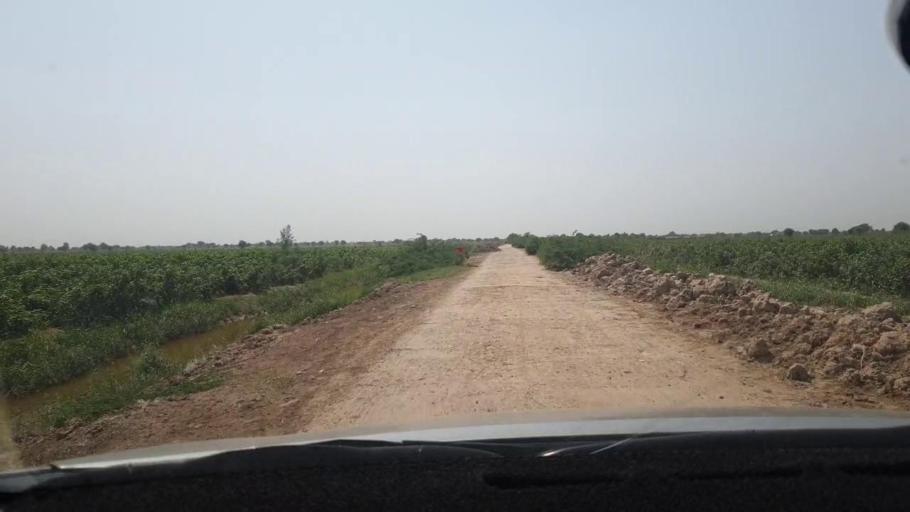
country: PK
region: Sindh
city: Tando Mittha Khan
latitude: 25.8534
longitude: 69.4175
